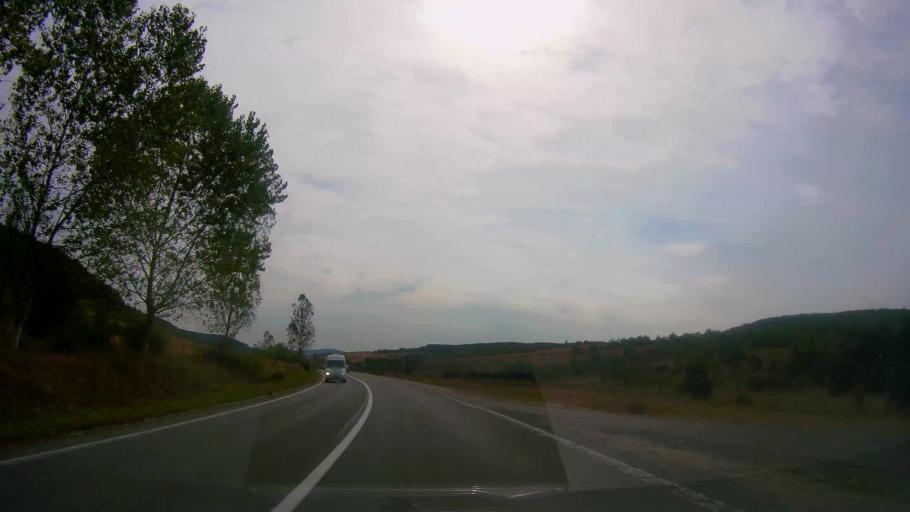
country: RO
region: Salaj
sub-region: Comuna Romanasi
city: Romanasi
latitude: 47.0592
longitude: 23.2157
